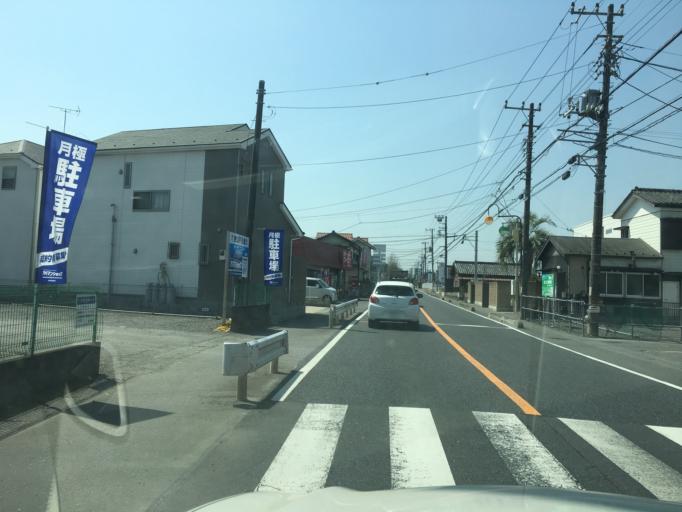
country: JP
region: Saitama
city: Sayama
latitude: 35.8317
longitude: 139.4224
